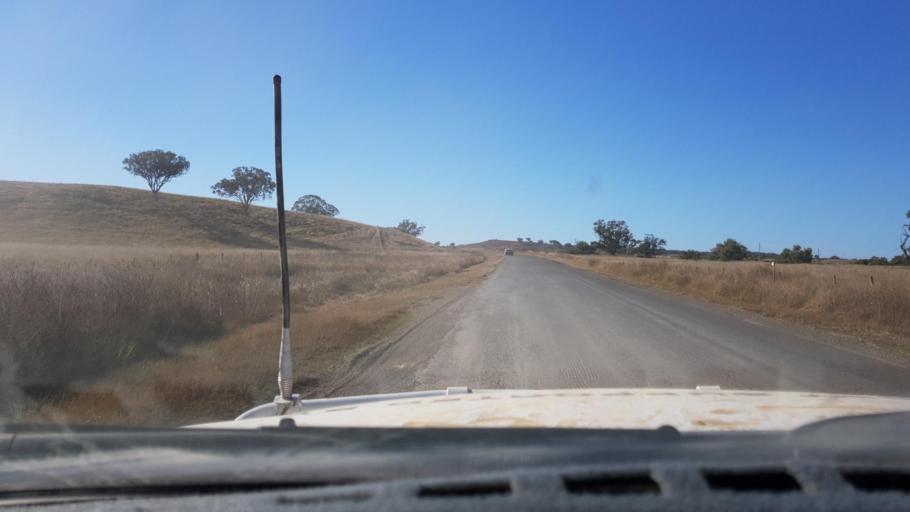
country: AU
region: New South Wales
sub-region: Narrabri
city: Blair Athol
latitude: -30.6762
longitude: 150.4220
